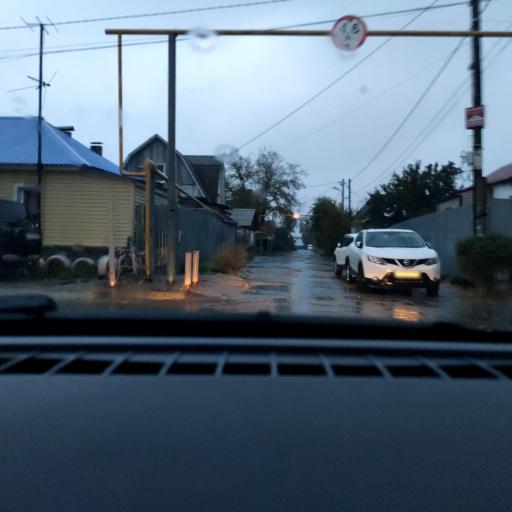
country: RU
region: Voronezj
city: Voronezh
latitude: 51.6752
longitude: 39.2443
